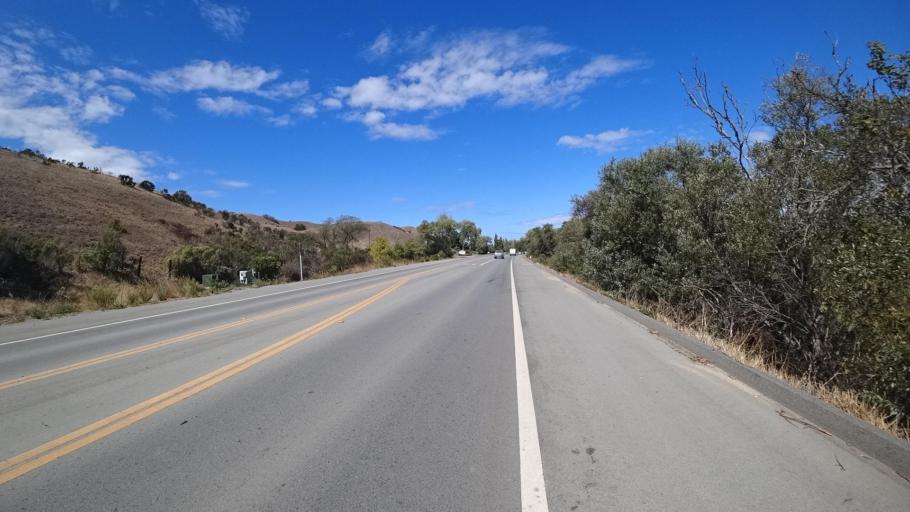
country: US
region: California
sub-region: Monterey County
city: Salinas
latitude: 36.6155
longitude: -121.6588
